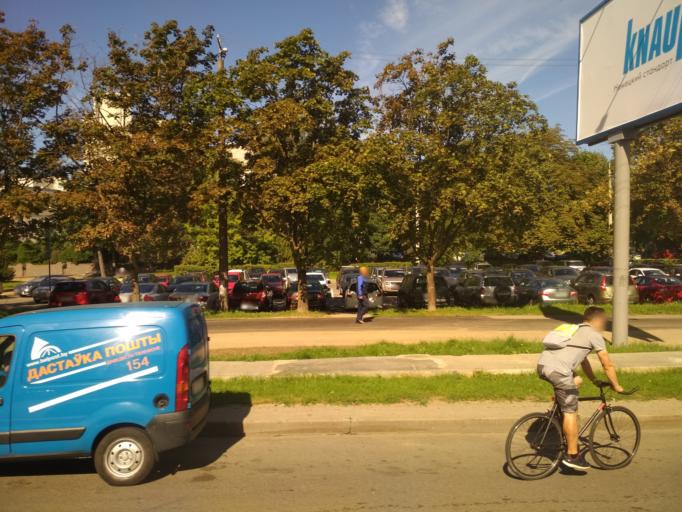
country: BY
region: Minsk
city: Minsk
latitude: 53.8962
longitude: 27.5419
